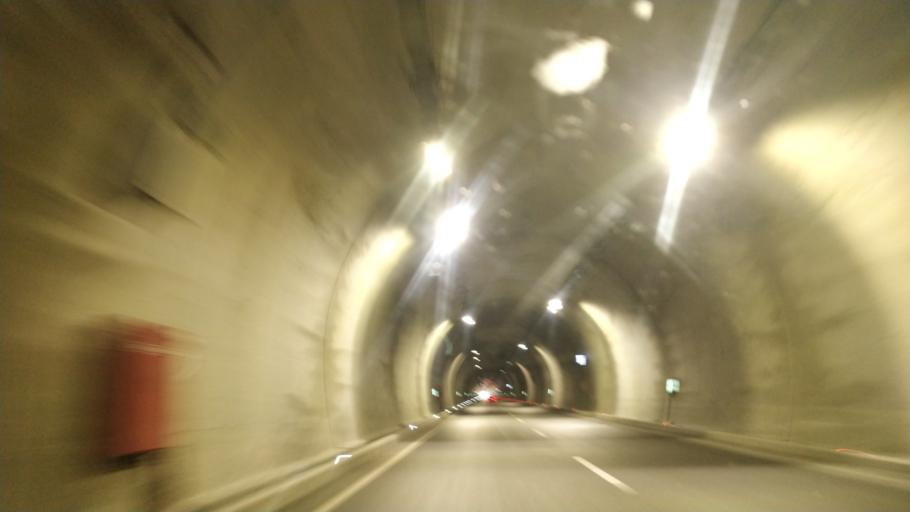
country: TR
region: Mersin
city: Aydincik
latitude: 36.1341
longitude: 33.2336
